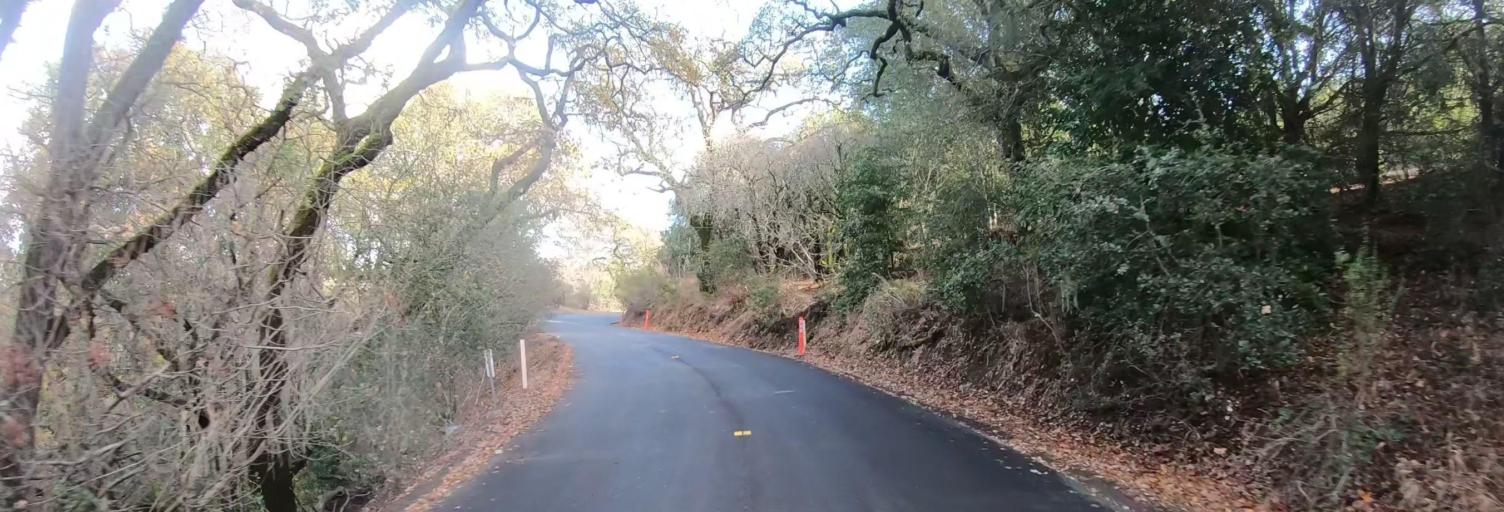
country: US
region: California
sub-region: Santa Clara County
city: East Foothills
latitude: 37.3593
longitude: -121.7532
